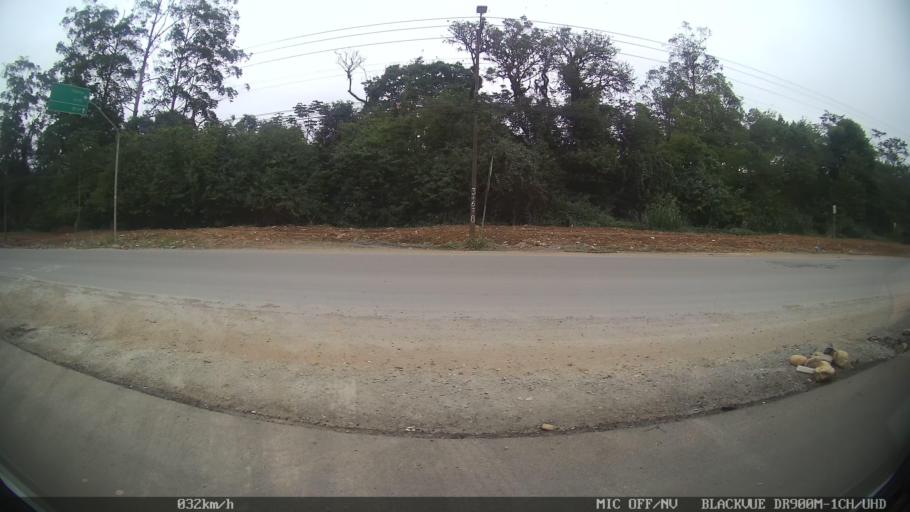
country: BR
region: Santa Catarina
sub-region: Joinville
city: Joinville
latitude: -26.2530
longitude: -48.8701
